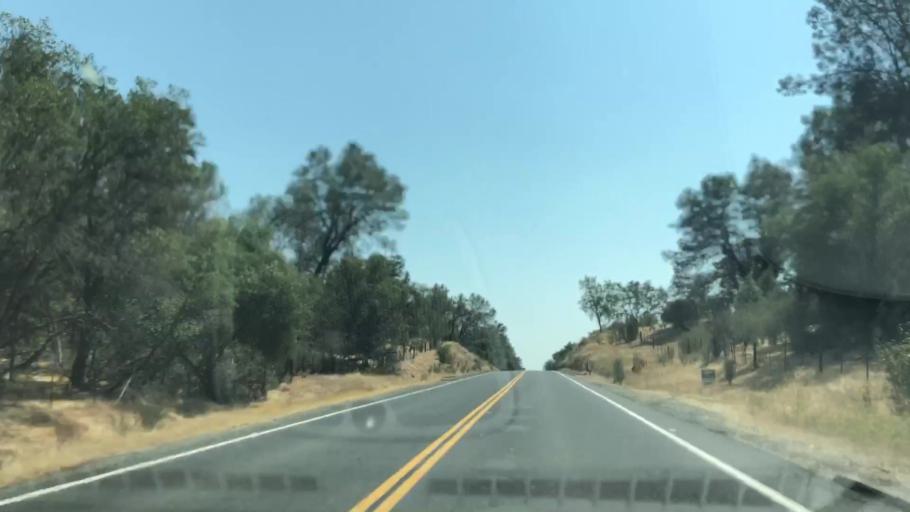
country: US
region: California
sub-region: Calaveras County
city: Copperopolis
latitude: 37.9479
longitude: -120.6100
